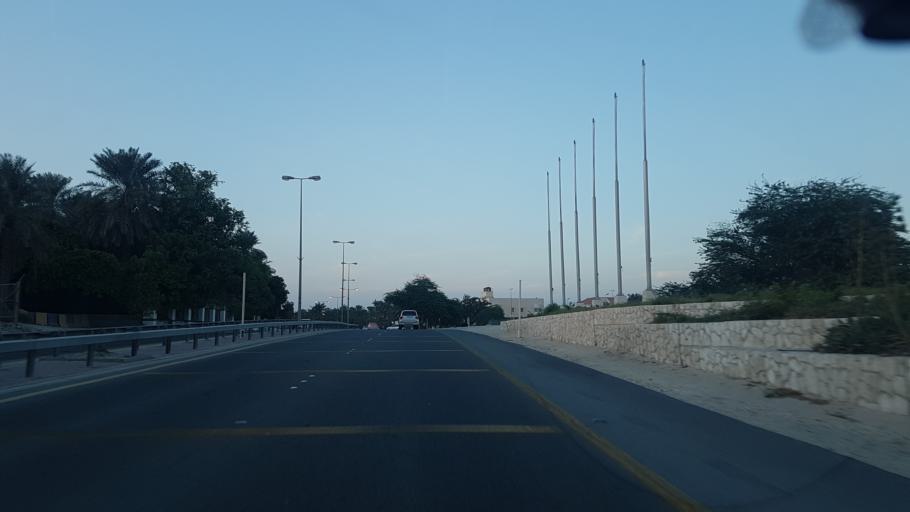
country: BH
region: Northern
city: Ar Rifa'
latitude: 26.1181
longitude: 50.5371
